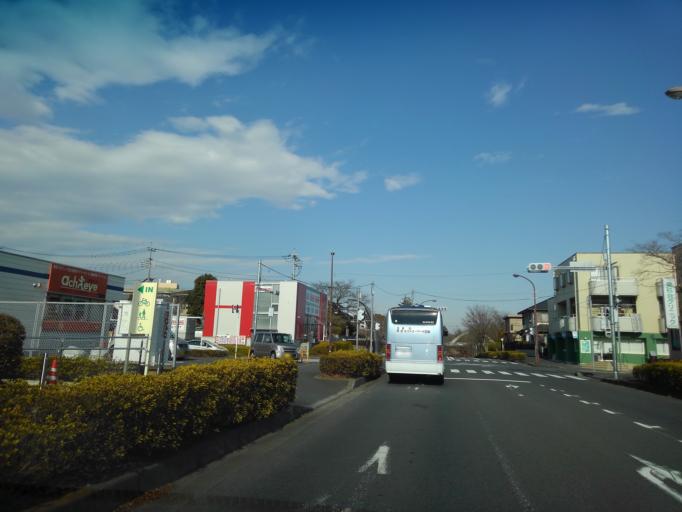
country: JP
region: Saitama
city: Hanno
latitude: 35.8416
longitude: 139.3105
